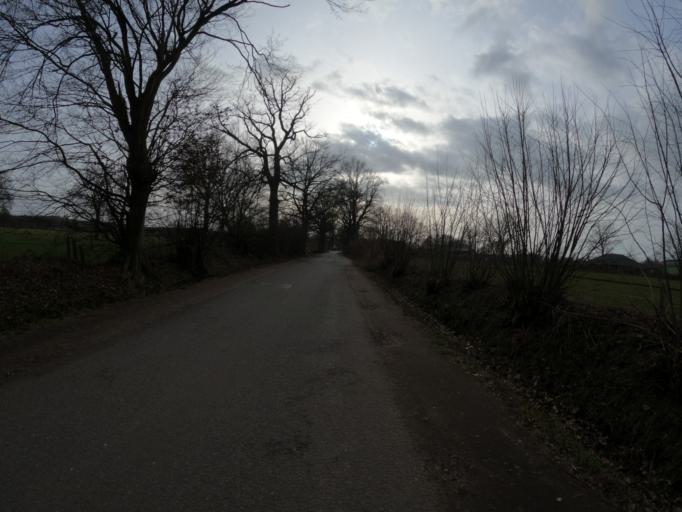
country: DE
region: Schleswig-Holstein
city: Rellingen
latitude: 53.5887
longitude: 9.7981
